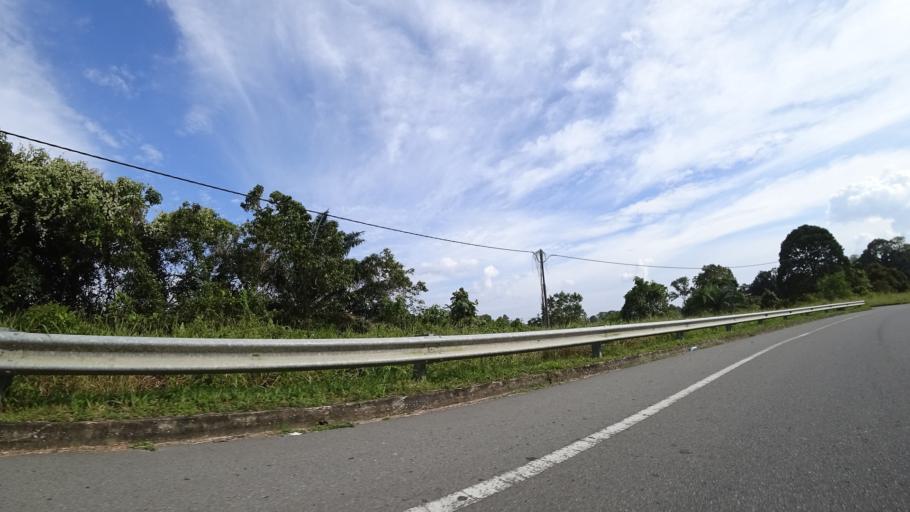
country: BN
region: Brunei and Muara
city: Bandar Seri Begawan
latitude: 4.8849
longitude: 114.8034
